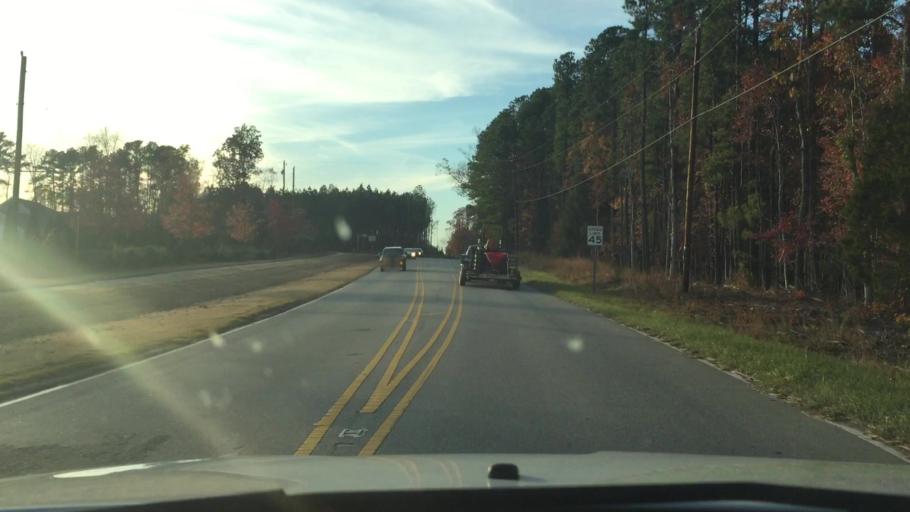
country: US
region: North Carolina
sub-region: Wake County
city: Green Level
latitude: 35.8453
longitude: -78.9150
